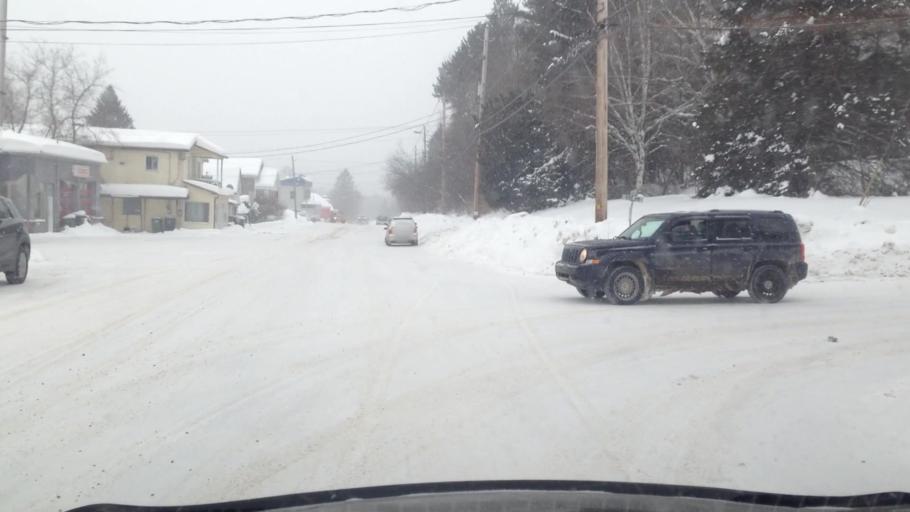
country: CA
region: Quebec
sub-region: Laurentides
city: Mont-Tremblant
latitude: 45.9743
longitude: -74.6345
